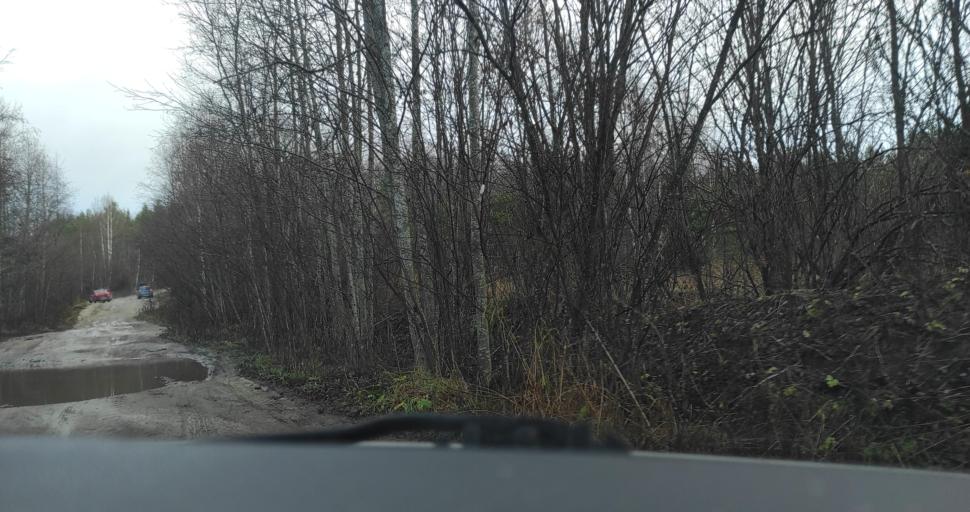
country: RU
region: Republic of Karelia
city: Pitkyaranta
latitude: 61.7352
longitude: 31.3866
